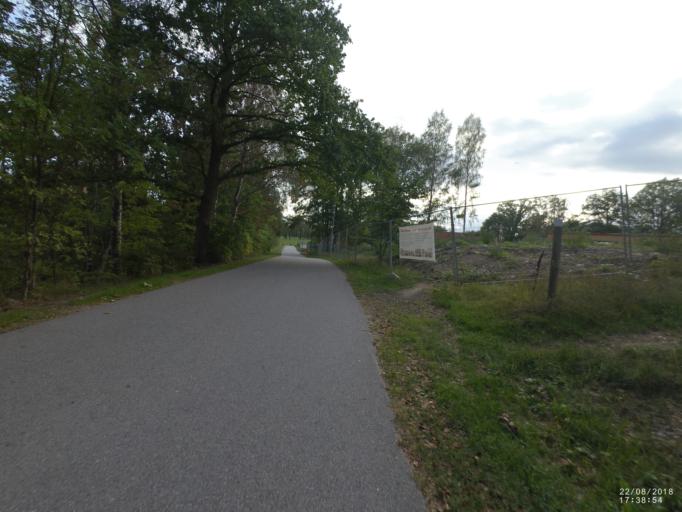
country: SE
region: Soedermanland
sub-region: Nykopings Kommun
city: Nykoping
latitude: 58.7609
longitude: 17.0052
